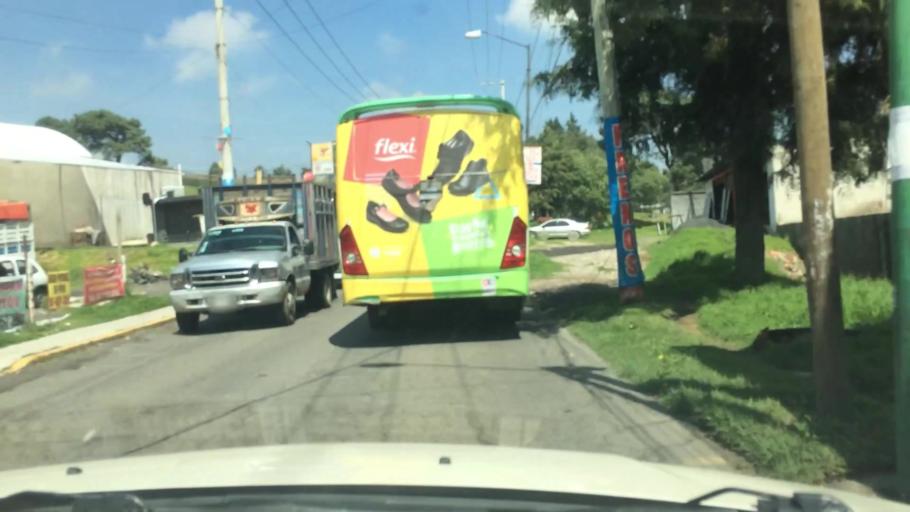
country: MX
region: Mexico City
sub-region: Tlalpan
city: Lomas de Tepemecatl
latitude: 19.2353
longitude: -99.1880
